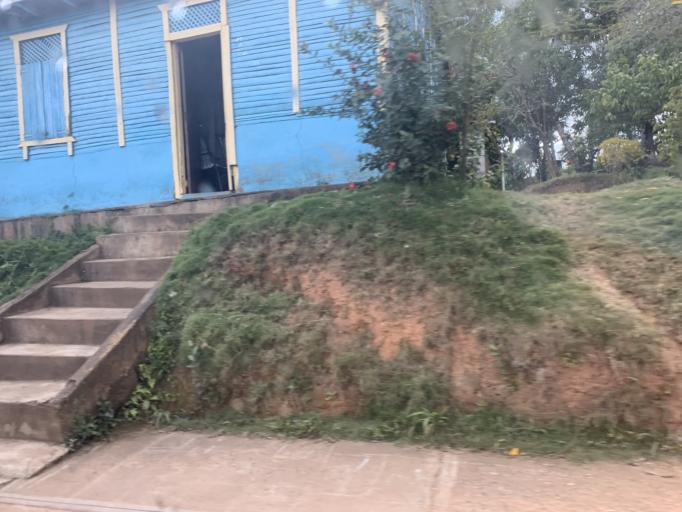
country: DO
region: Monte Plata
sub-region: Yamasa
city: Yamasa
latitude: 18.7721
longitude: -70.0199
